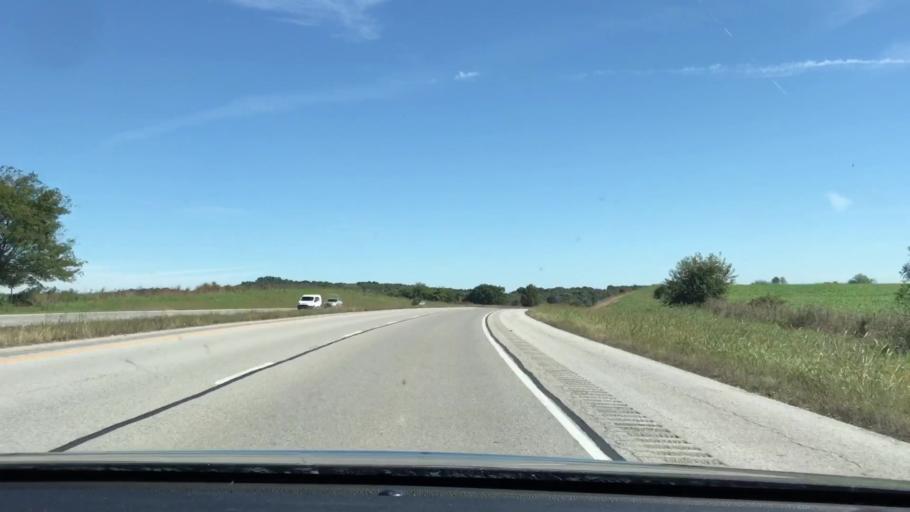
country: US
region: Kentucky
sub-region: Logan County
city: Auburn
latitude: 36.8901
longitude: -86.6544
